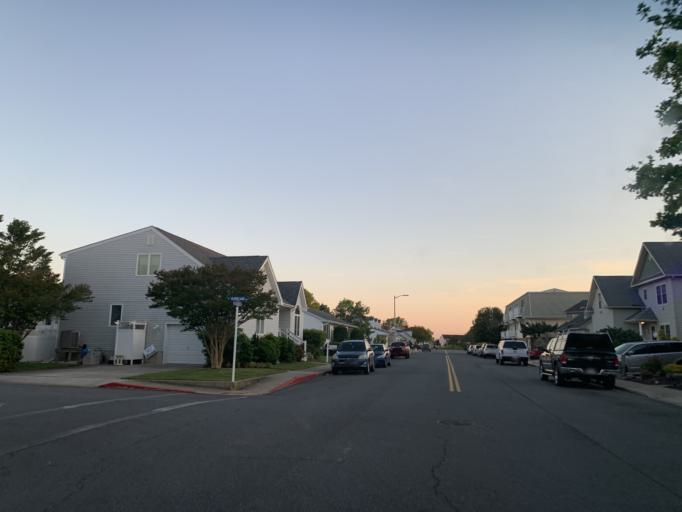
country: US
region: Delaware
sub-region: Sussex County
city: Bethany Beach
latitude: 38.4507
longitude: -75.0646
